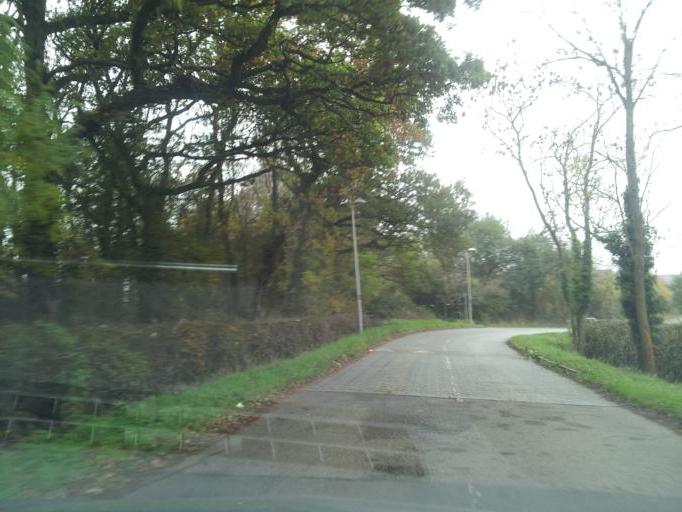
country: GB
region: England
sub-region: Milton Keynes
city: Shenley Church End
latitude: 51.9957
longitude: -0.8062
